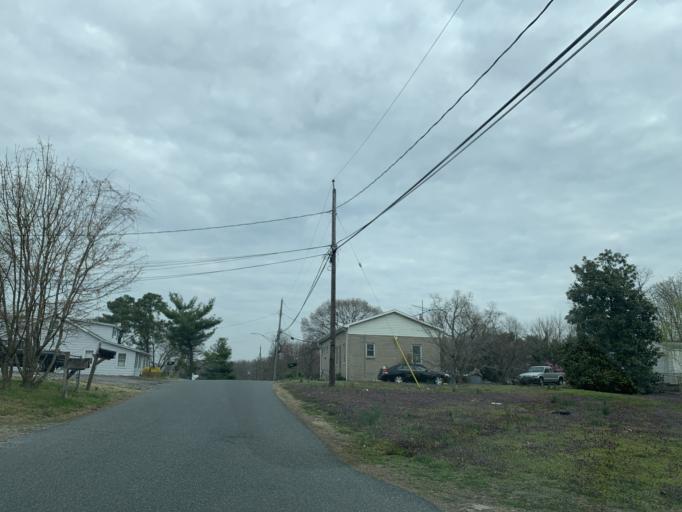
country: US
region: Maryland
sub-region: Baltimore County
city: Edgemere
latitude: 39.2551
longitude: -76.4361
